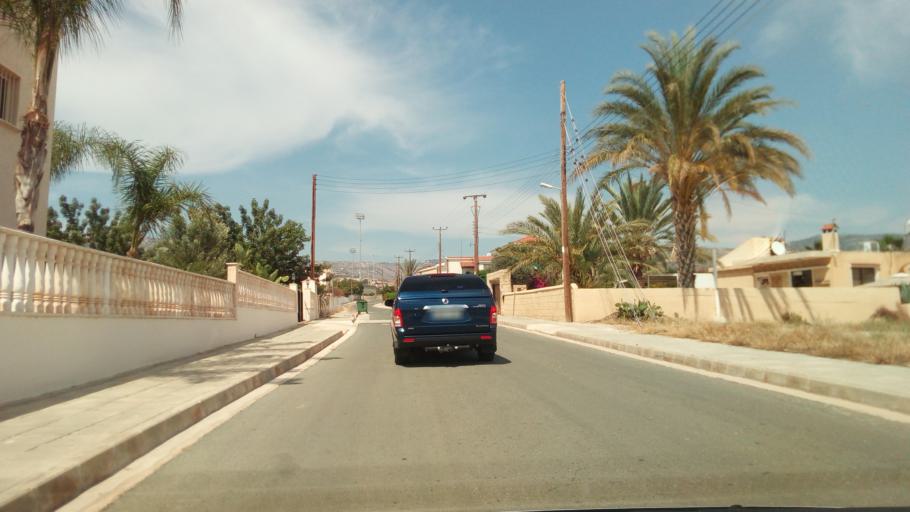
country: CY
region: Pafos
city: Pegeia
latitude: 34.8724
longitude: 32.3804
